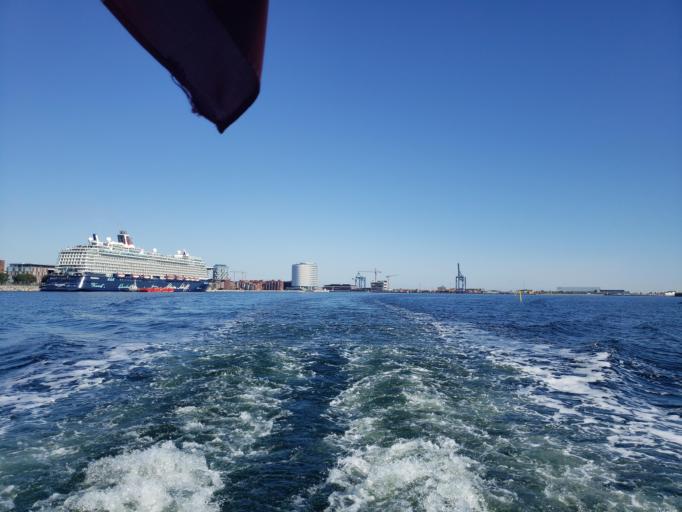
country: DK
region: Capital Region
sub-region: Kobenhavn
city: Christianshavn
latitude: 55.6963
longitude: 12.6056
